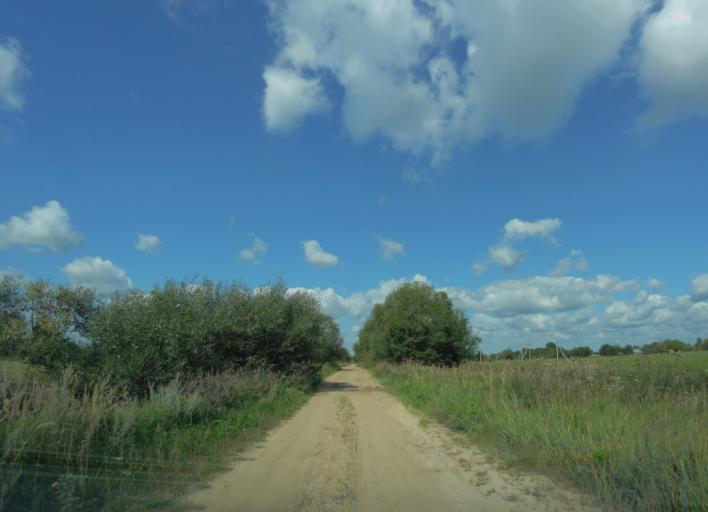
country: BY
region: Minsk
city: Zyembin
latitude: 54.4132
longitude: 28.3773
